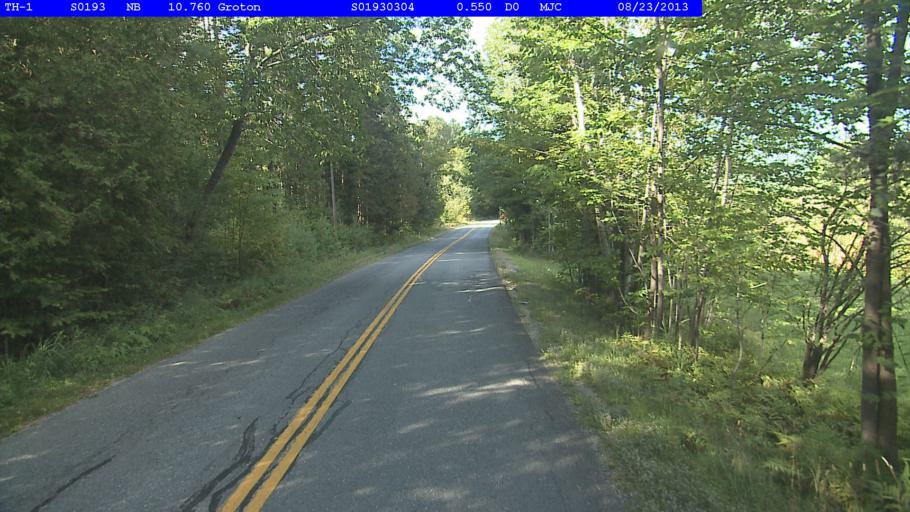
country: US
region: New Hampshire
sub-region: Grafton County
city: Woodsville
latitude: 44.1954
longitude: -72.2146
